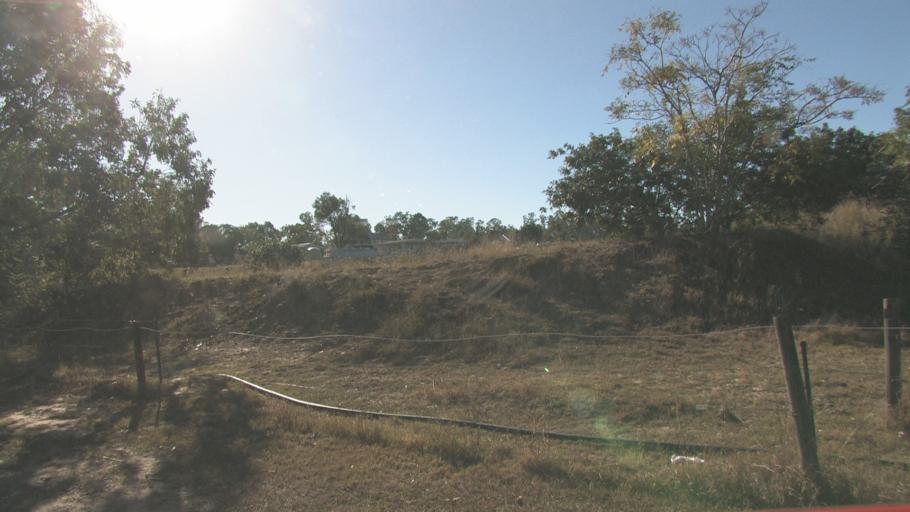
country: AU
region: Queensland
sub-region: Logan
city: North Maclean
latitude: -27.7603
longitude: 153.0329
